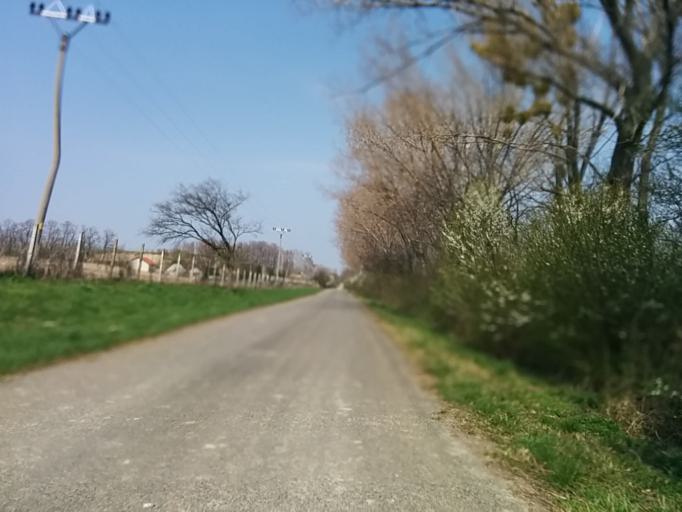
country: SK
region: Trnavsky
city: Sladkovicovo
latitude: 48.2588
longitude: 17.6165
